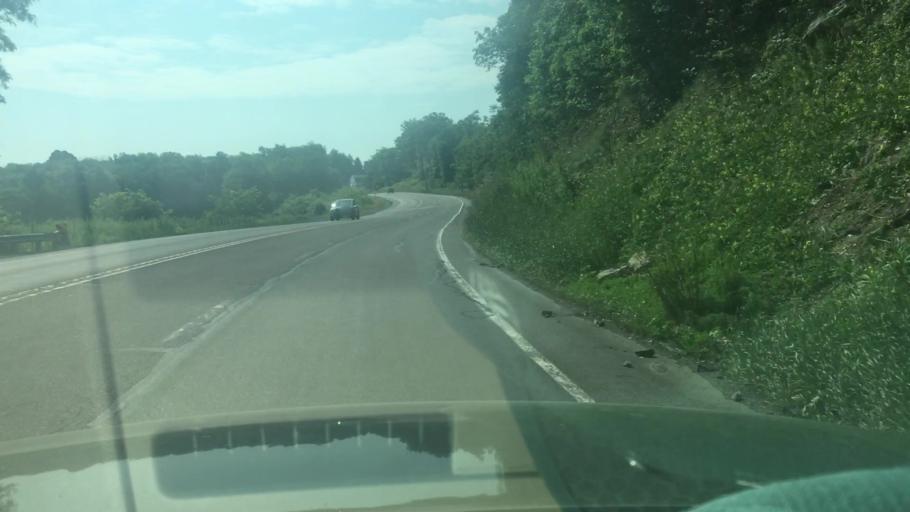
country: US
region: Pennsylvania
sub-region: Northumberland County
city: Kulpmont
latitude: 40.8203
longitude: -76.4686
